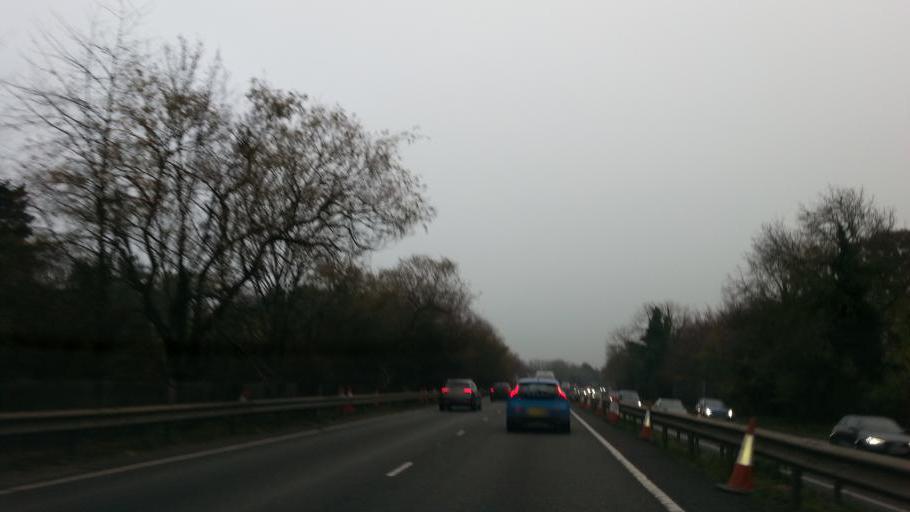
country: GB
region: England
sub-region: Cambridgeshire
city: Hemingford Grey
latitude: 52.3008
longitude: -0.0824
